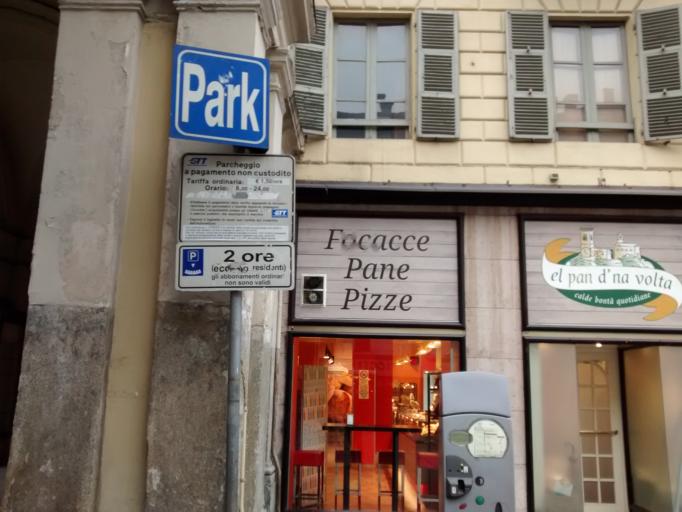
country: IT
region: Piedmont
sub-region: Provincia di Torino
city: Turin
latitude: 45.0640
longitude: 7.6789
